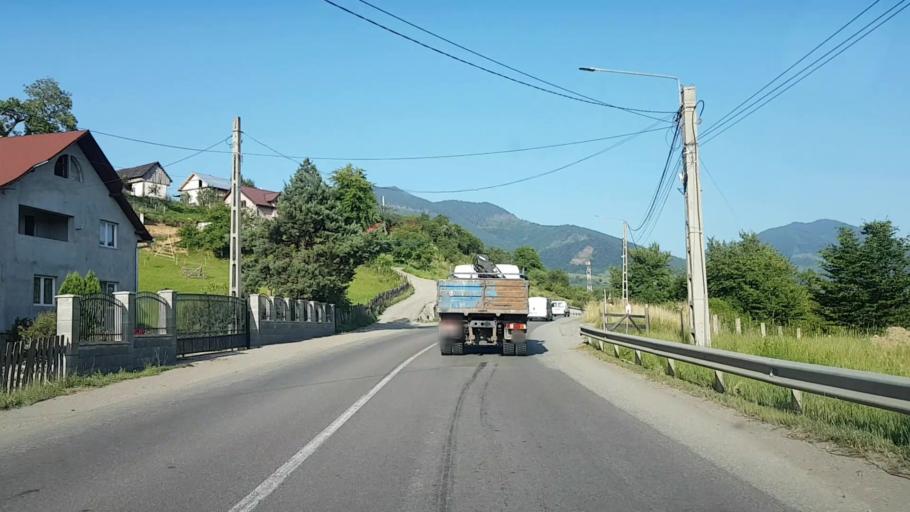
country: RO
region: Bistrita-Nasaud
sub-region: Comuna Tiha Bargaului
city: Tureac
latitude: 47.2298
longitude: 24.7990
